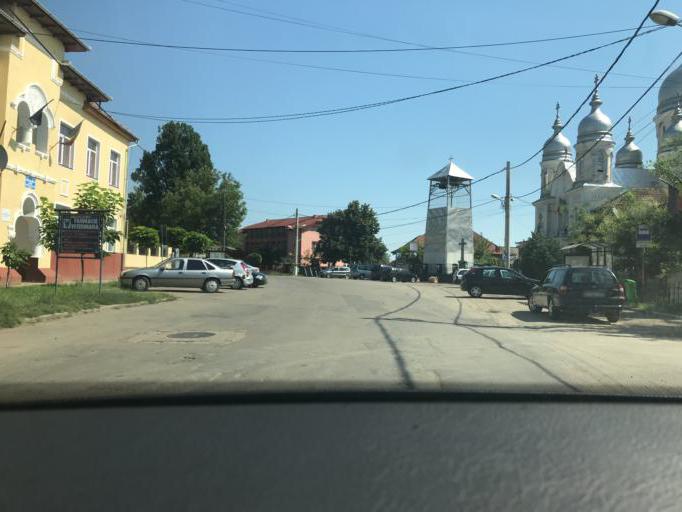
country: RO
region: Bihor
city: Margita
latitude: 47.3447
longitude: 22.3410
